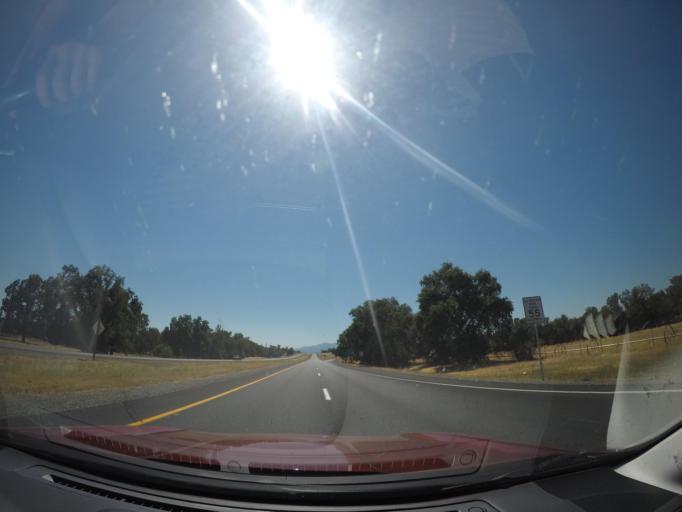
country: US
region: California
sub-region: Shasta County
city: Bella Vista
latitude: 40.6223
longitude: -122.3122
